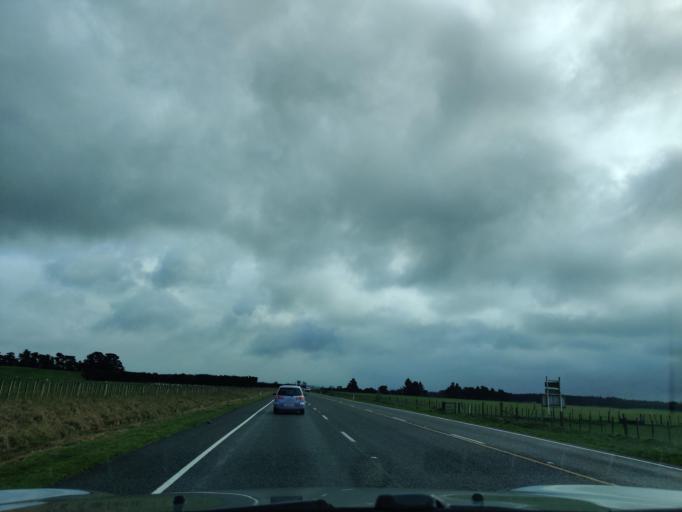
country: NZ
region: Hawke's Bay
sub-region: Hastings District
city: Hastings
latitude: -40.0208
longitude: 176.3100
